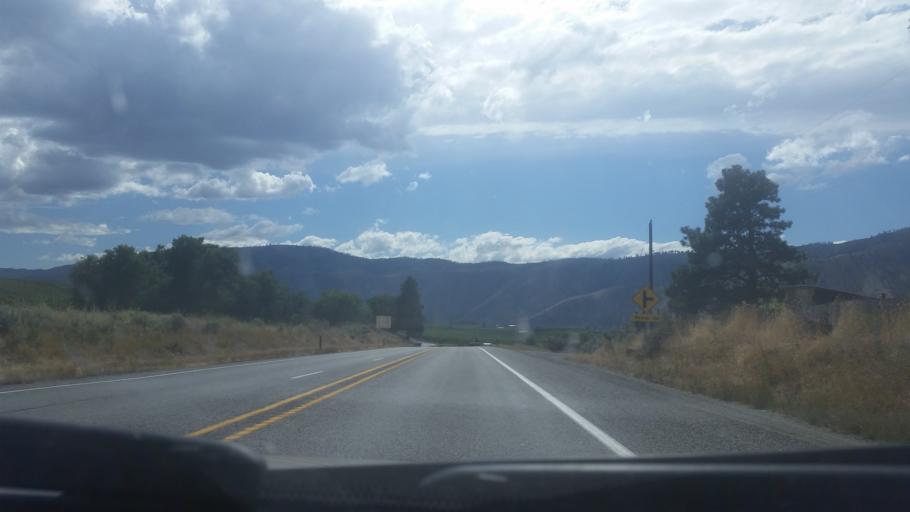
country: US
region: Washington
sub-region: Chelan County
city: Entiat
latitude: 47.7514
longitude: -120.1770
